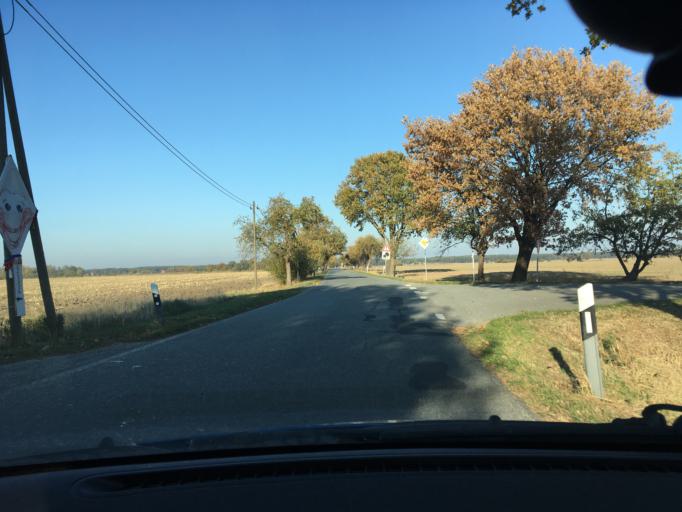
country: DE
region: Lower Saxony
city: Hitzacker
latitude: 53.1719
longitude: 11.0384
